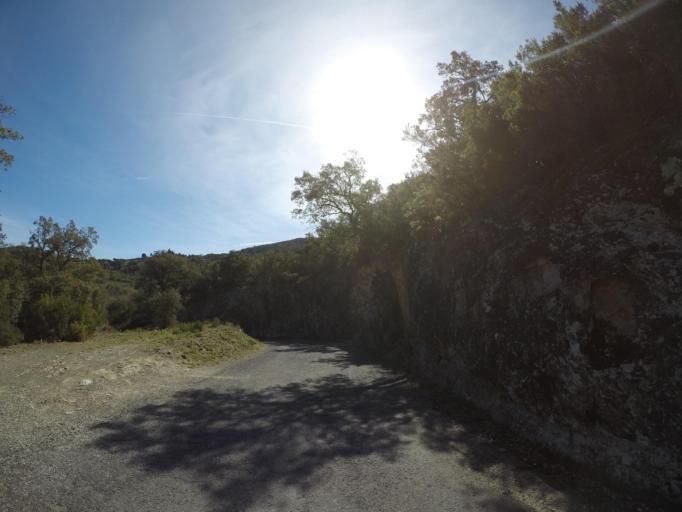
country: FR
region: Languedoc-Roussillon
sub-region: Departement des Pyrenees-Orientales
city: Thuir
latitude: 42.6240
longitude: 2.7060
